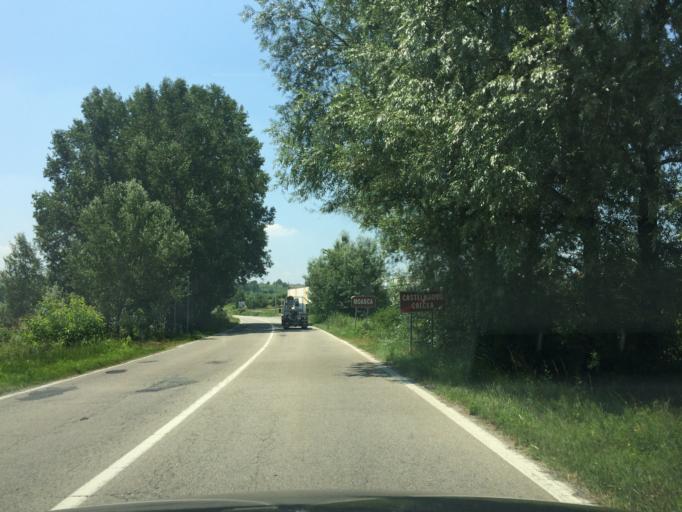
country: IT
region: Piedmont
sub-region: Provincia di Asti
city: Moasca
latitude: 44.7736
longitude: 8.2718
